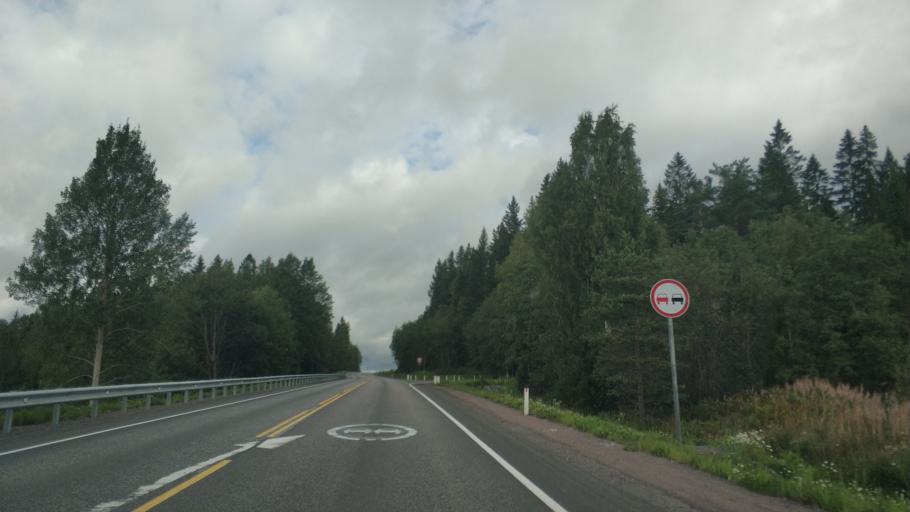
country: RU
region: Republic of Karelia
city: Khelyulya
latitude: 61.7931
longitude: 30.6269
